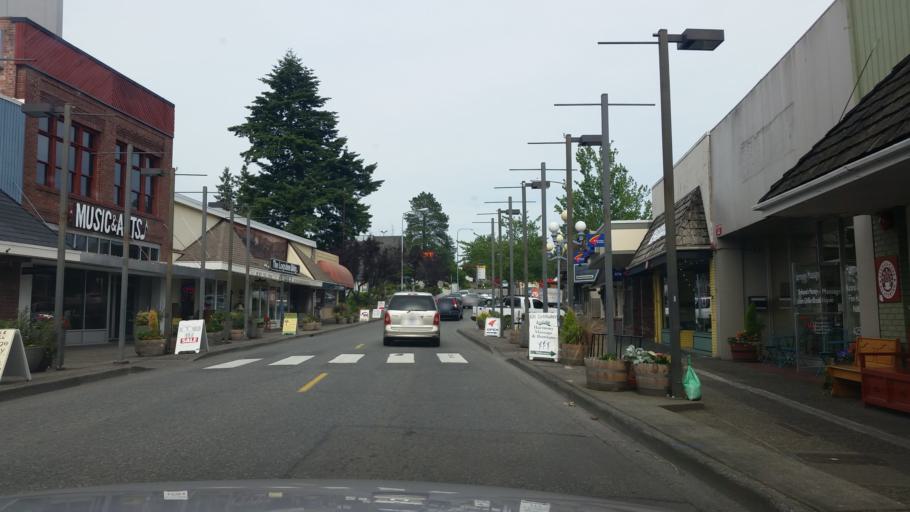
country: US
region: Washington
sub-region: King County
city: Bothell
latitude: 47.7601
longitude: -122.2049
